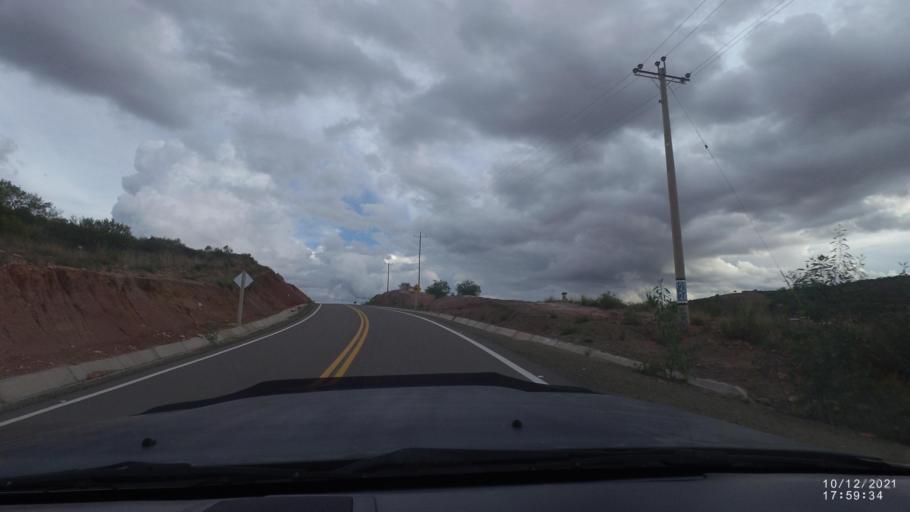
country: BO
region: Cochabamba
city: Cliza
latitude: -17.7347
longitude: -65.9254
